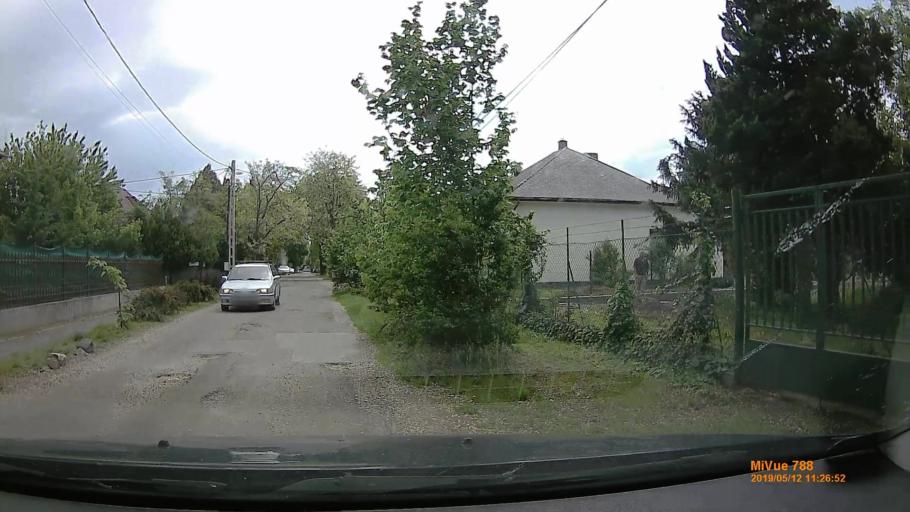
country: HU
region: Budapest
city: Budapest XVII. keruelet
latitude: 47.4660
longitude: 19.2433
